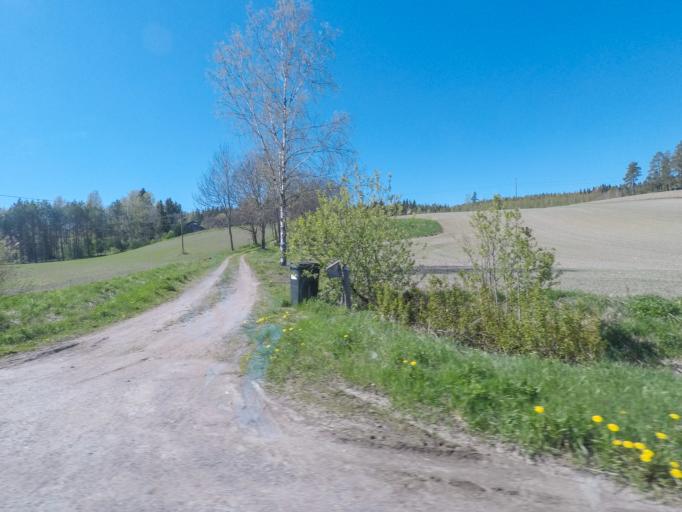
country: FI
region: Uusimaa
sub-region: Helsinki
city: Sammatti
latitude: 60.4139
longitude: 23.8252
